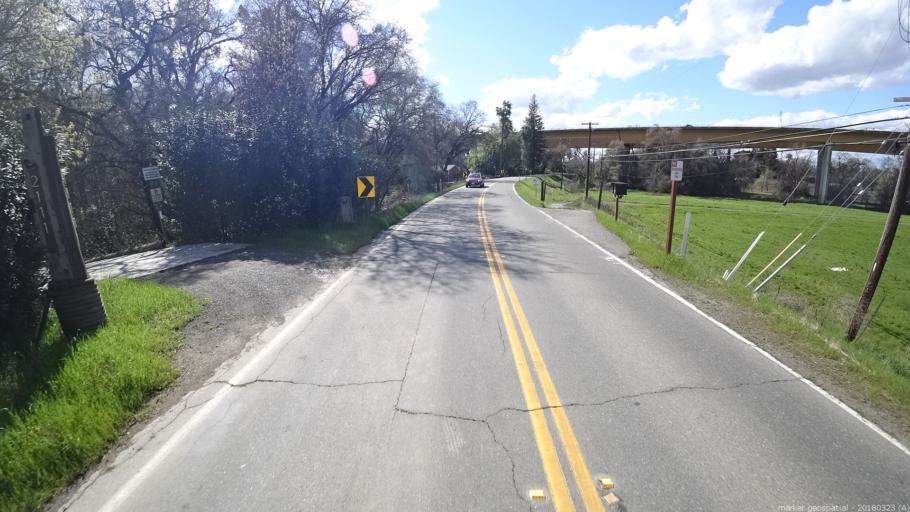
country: US
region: California
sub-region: Yolo County
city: West Sacramento
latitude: 38.5996
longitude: -121.5453
